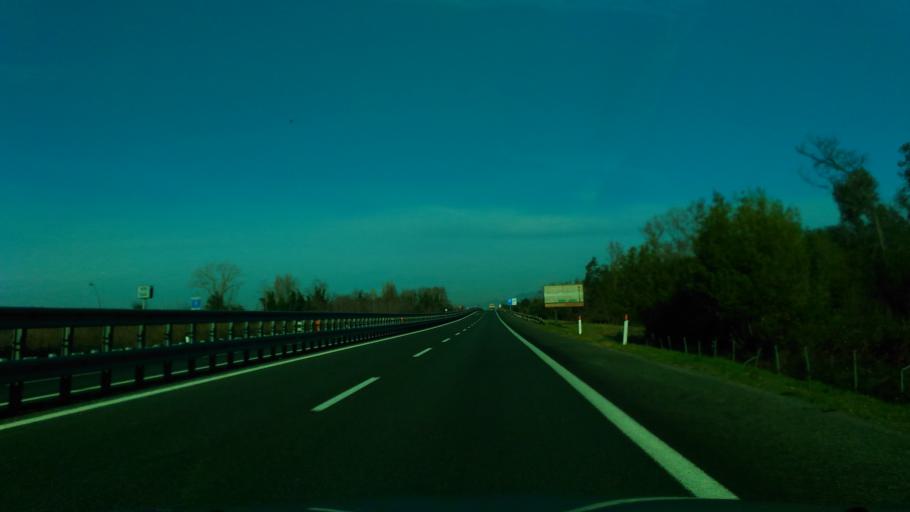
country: IT
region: Tuscany
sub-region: Provincia di Lucca
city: Torre del Lago Puccini
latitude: 43.8228
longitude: 10.3061
